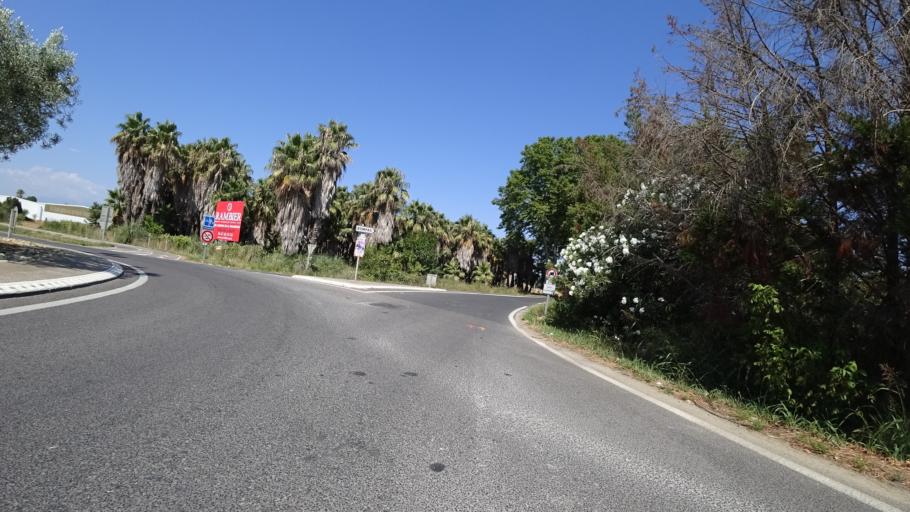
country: FR
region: Languedoc-Roussillon
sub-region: Departement des Pyrenees-Orientales
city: Bompas
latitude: 42.7266
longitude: 2.9466
